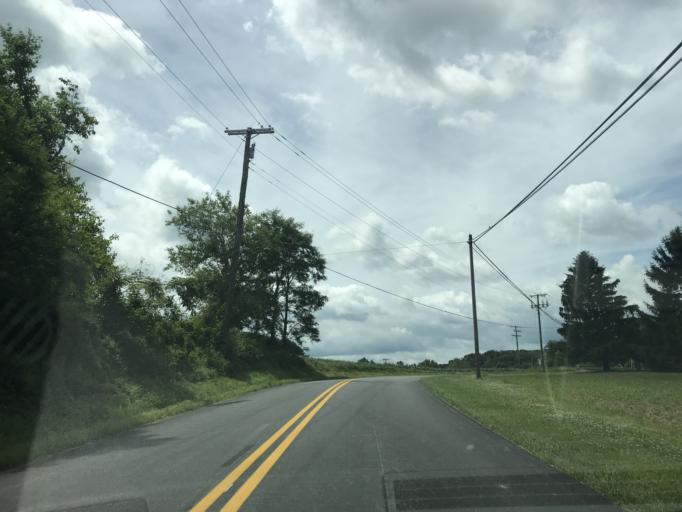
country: US
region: Maryland
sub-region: Carroll County
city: Hampstead
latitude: 39.6138
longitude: -76.7982
